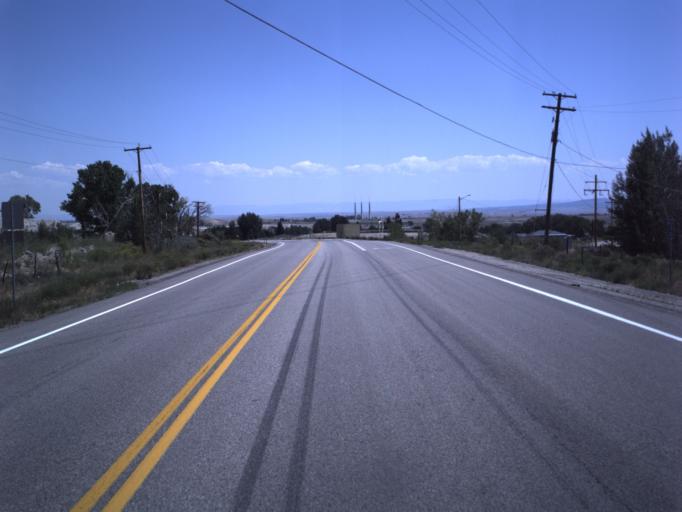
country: US
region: Utah
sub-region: Emery County
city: Ferron
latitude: 39.1273
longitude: -111.1052
